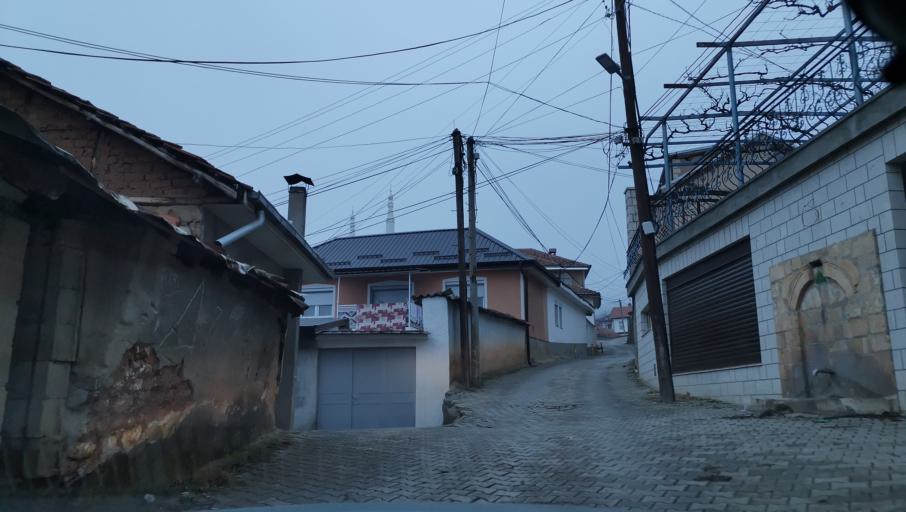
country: MK
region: Debar
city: Debar
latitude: 41.5254
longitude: 20.5279
